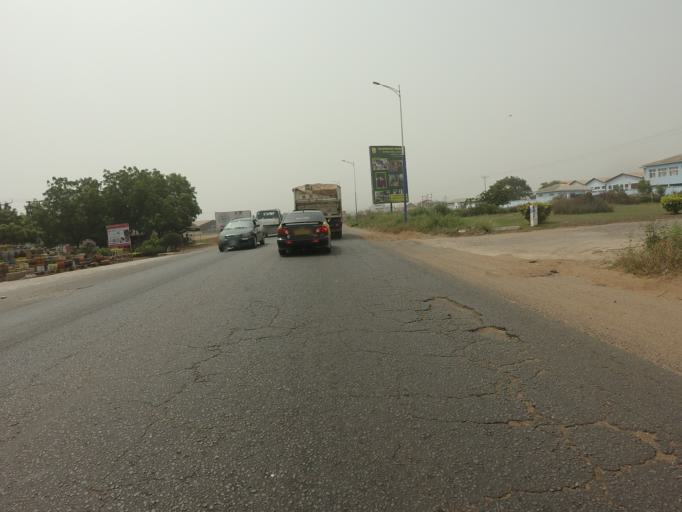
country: GH
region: Greater Accra
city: Tema
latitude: 5.7251
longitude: 0.0221
